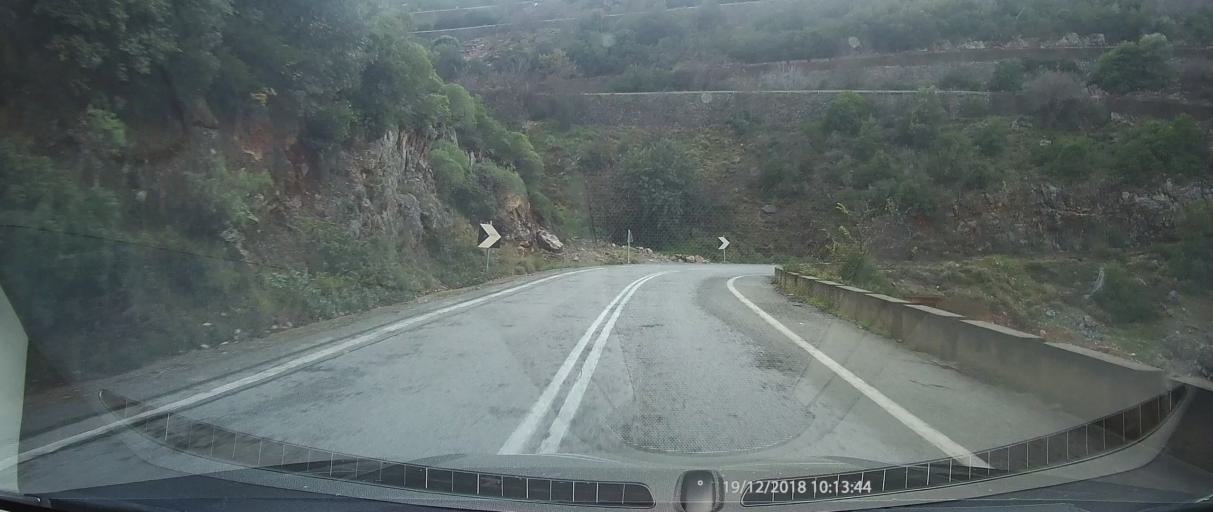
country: GR
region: Peloponnese
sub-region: Nomos Messinias
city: Kalamata
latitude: 37.0836
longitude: 22.1577
